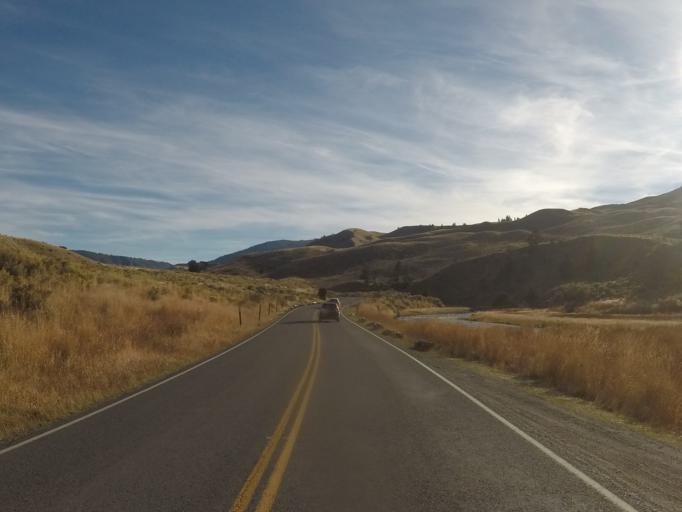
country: US
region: Montana
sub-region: Gallatin County
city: West Yellowstone
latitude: 44.9963
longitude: -110.6933
